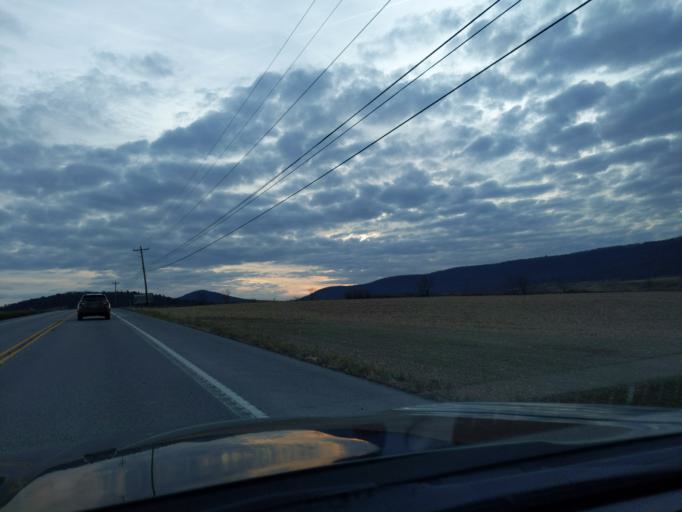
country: US
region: Pennsylvania
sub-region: Blair County
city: Williamsburg
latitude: 40.5236
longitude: -78.2011
